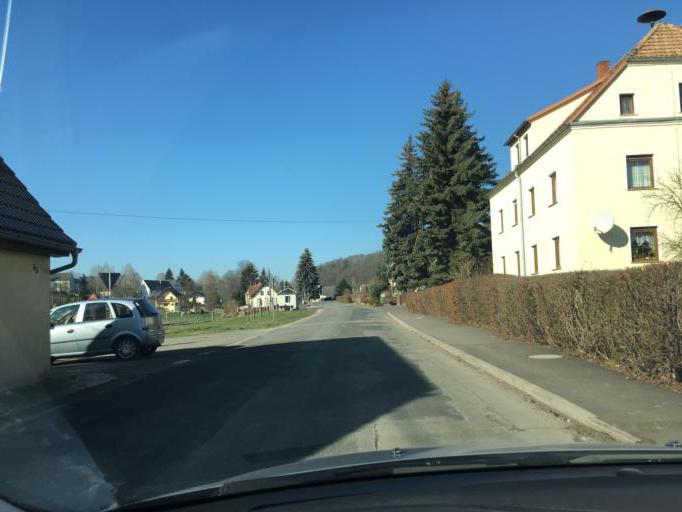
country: DE
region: Saxony
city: Lunzenau
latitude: 50.9661
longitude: 12.7278
